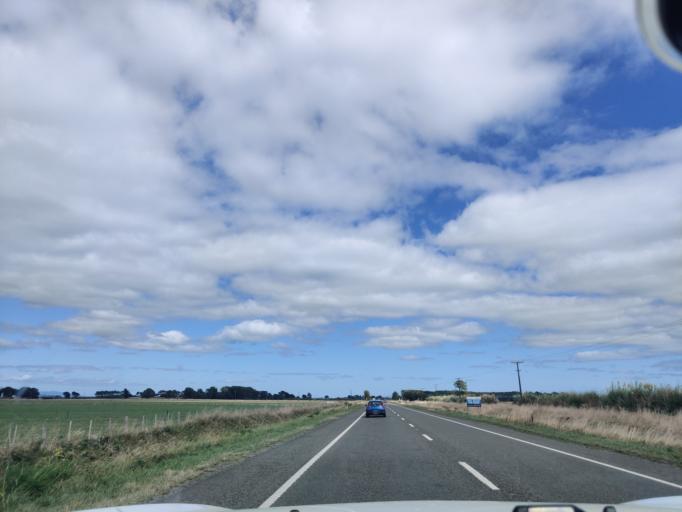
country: NZ
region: Manawatu-Wanganui
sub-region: Palmerston North City
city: Palmerston North
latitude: -40.4061
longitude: 175.4929
